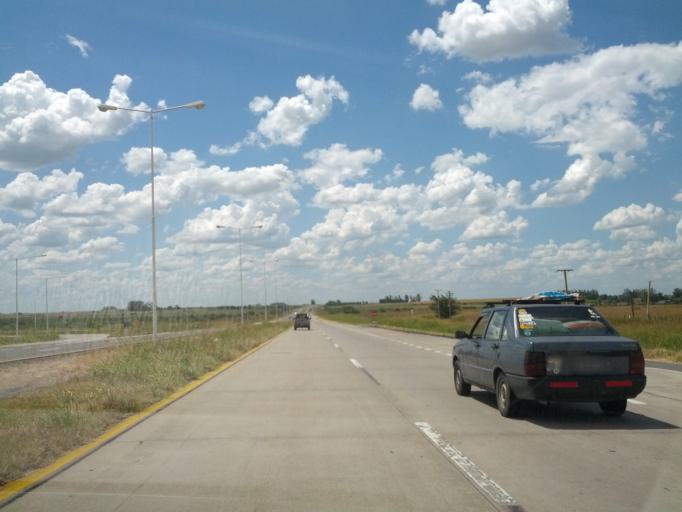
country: AR
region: Entre Rios
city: Gualeguaychu
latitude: -32.8961
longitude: -58.5520
